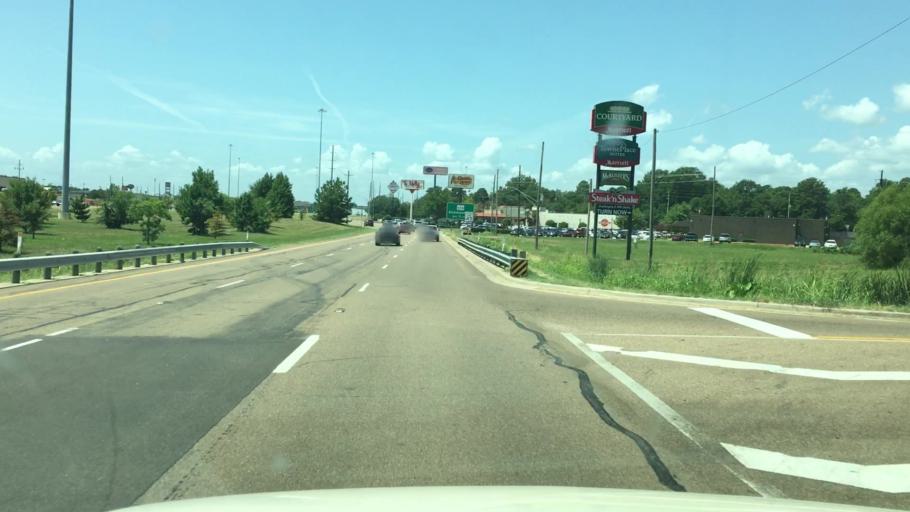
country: US
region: Texas
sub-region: Bowie County
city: Wake Village
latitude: 33.4607
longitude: -94.0789
